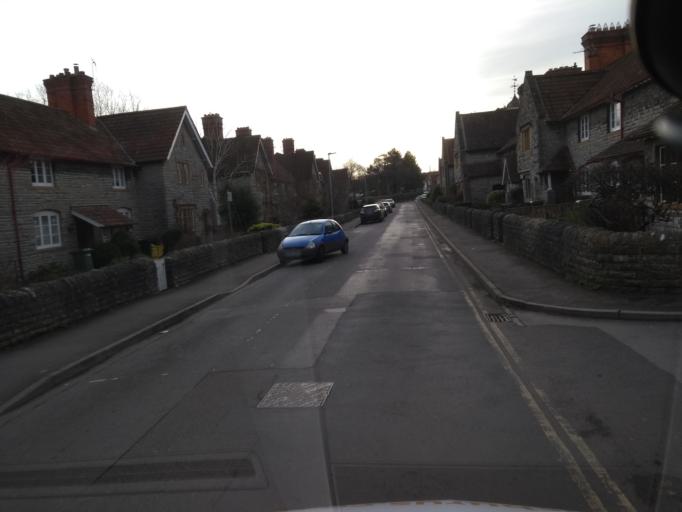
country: GB
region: England
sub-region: Somerset
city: Street
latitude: 51.1274
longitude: -2.7372
